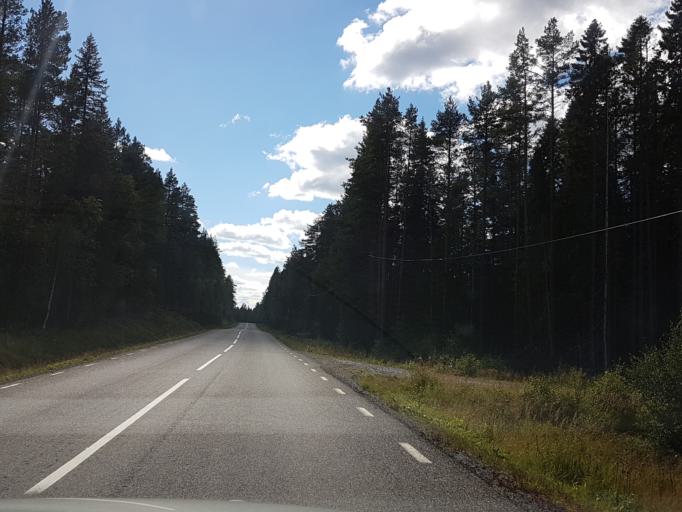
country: SE
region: Vaesterbotten
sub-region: Umea Kommun
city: Saevar
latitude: 64.1324
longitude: 20.5553
